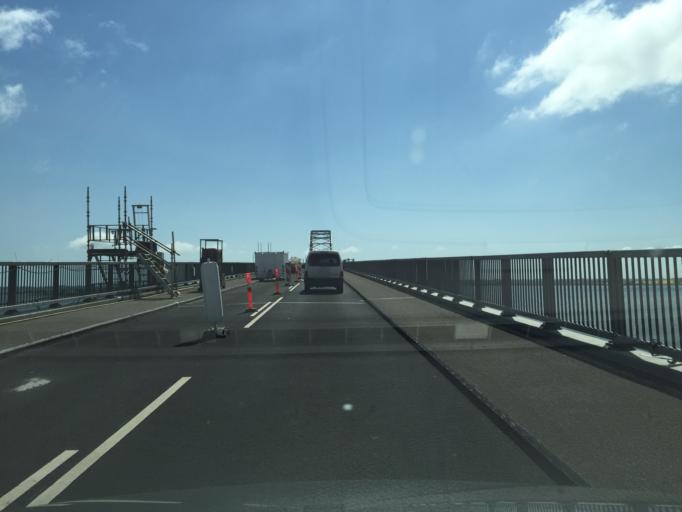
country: DK
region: Zealand
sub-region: Vordingborg Kommune
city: Stege
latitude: 54.9918
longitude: 12.1619
